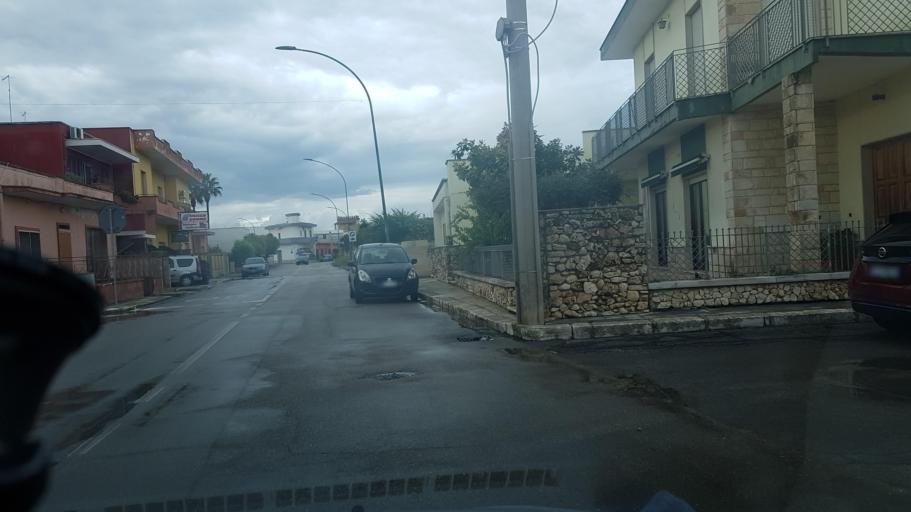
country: IT
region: Apulia
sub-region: Provincia di Lecce
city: Guagnano
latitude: 40.3956
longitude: 17.9545
